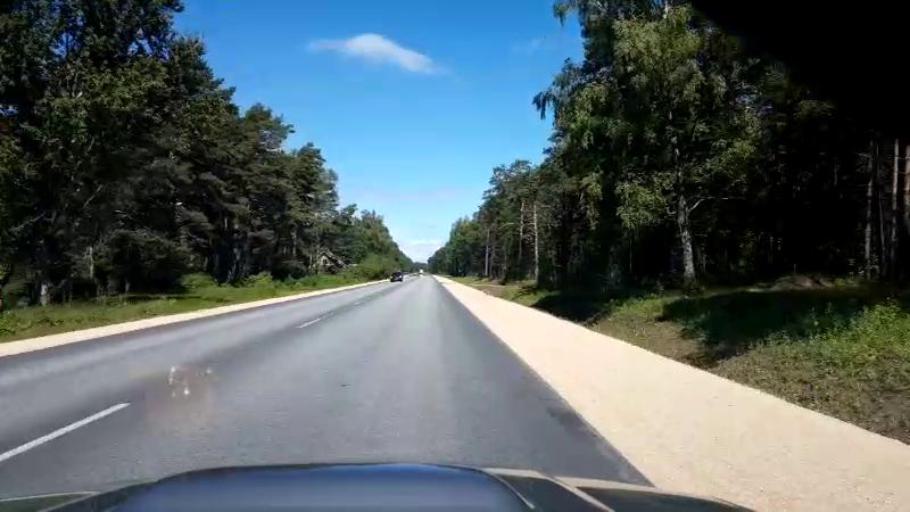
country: LV
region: Salacgrivas
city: Salacgriva
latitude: 57.8016
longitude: 24.3496
